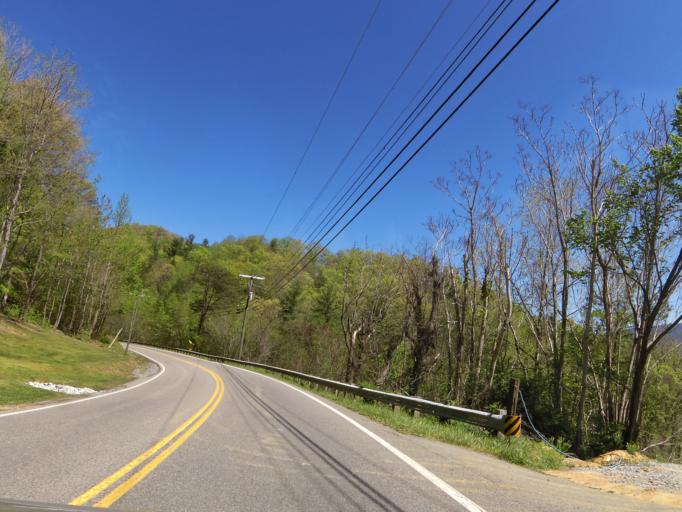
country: US
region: Tennessee
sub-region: Unicoi County
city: Banner Hill
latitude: 36.1436
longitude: -82.4396
